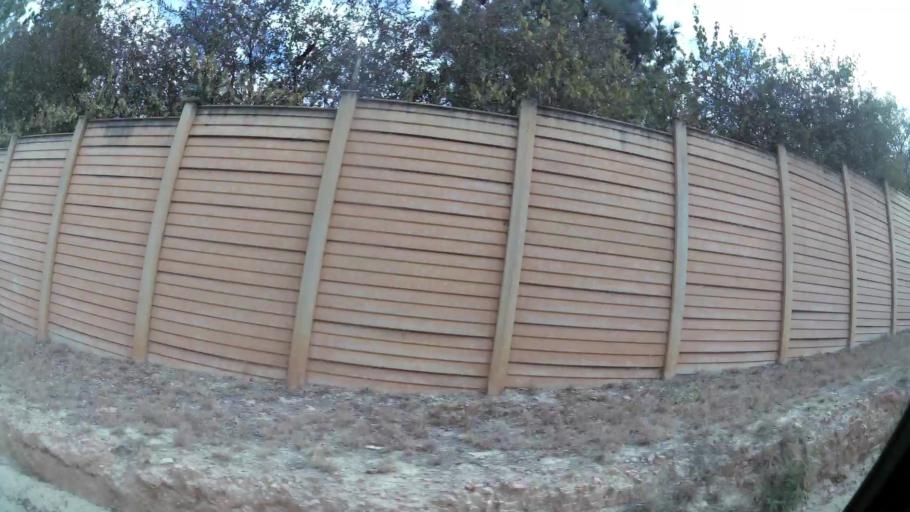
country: ZA
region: Gauteng
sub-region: West Rand District Municipality
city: Muldersdriseloop
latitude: -26.0783
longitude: 27.8790
